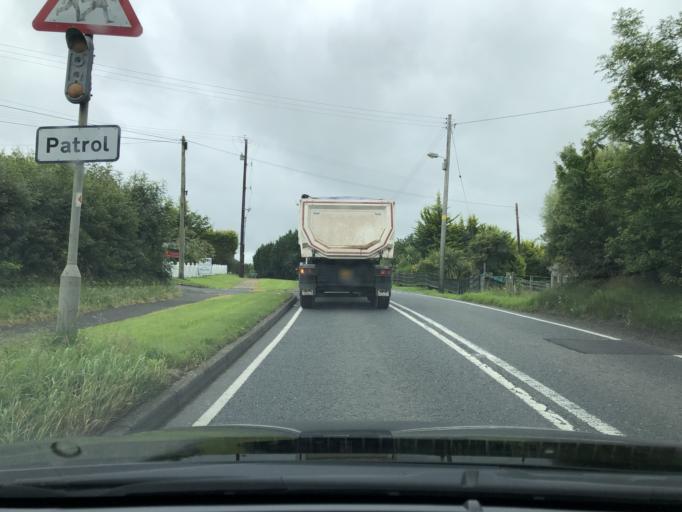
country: GB
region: Northern Ireland
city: Ballynahinch
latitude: 54.3664
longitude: -5.8607
